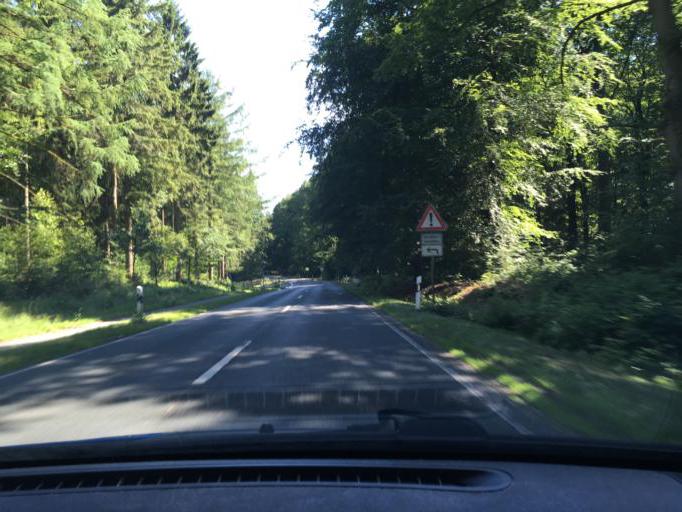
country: DE
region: Lower Saxony
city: Bendestorf
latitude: 53.3445
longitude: 9.9416
